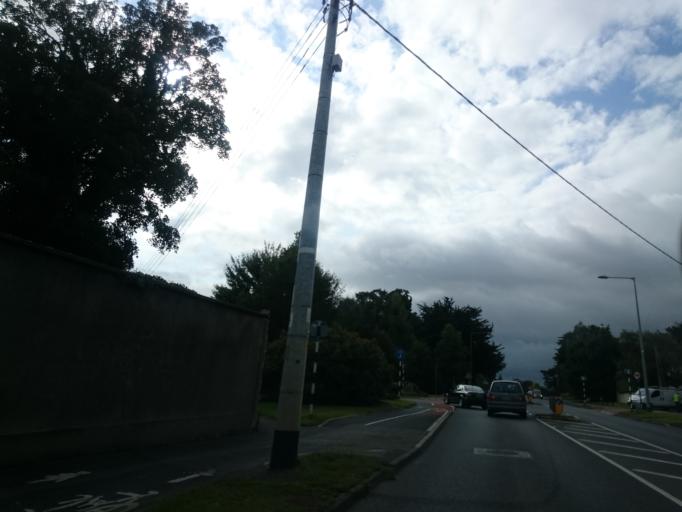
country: IE
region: Leinster
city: Mount Merrion
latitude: 53.2909
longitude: -6.2279
